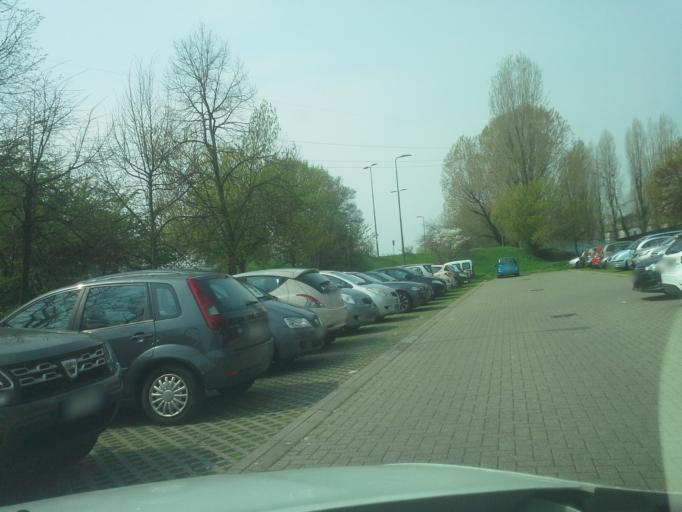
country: IT
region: Lombardy
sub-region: Citta metropolitana di Milano
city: Cesano Boscone
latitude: 45.4557
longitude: 9.0880
